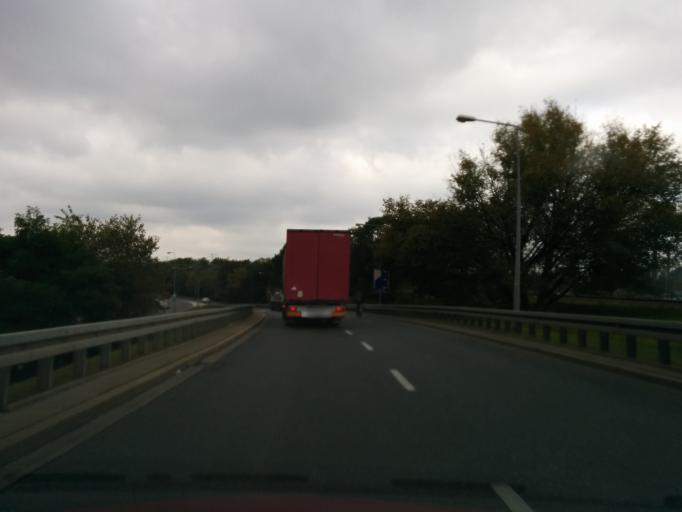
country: PL
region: Masovian Voivodeship
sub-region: Warszawa
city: Praga Polnoc
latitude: 52.2680
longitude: 21.0357
